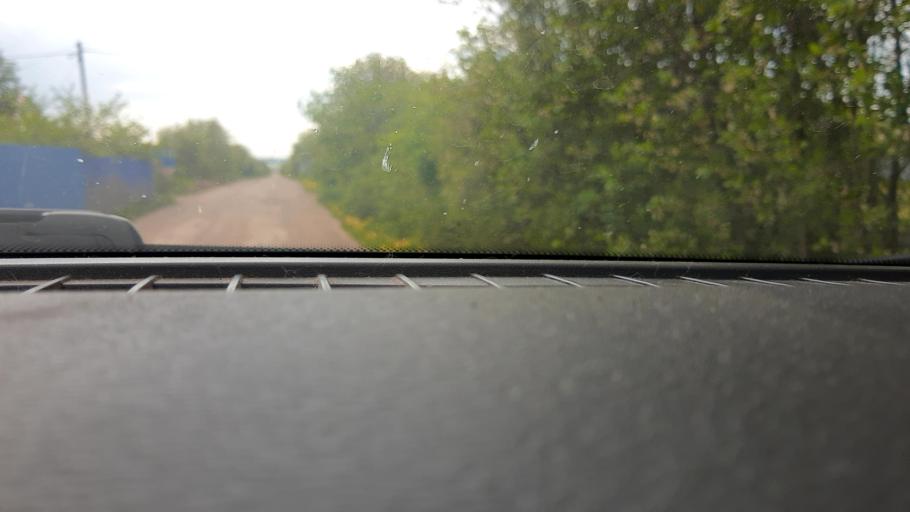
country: RU
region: Bashkortostan
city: Avdon
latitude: 54.5688
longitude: 55.7412
